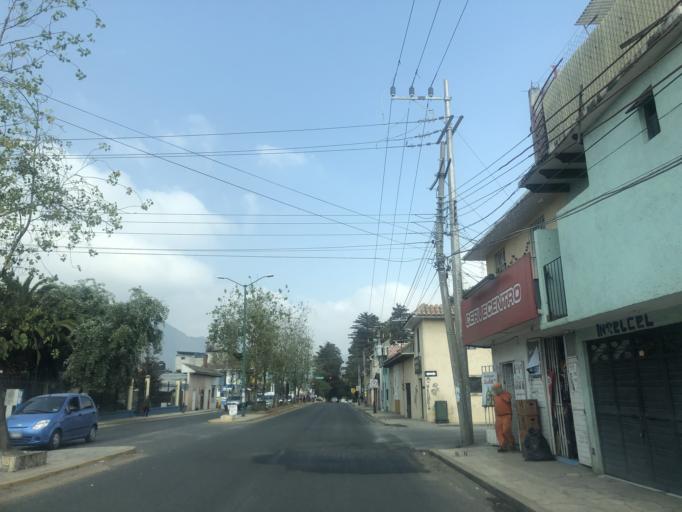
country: MX
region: Chiapas
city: San Cristobal de las Casas
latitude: 16.7211
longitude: -92.6387
